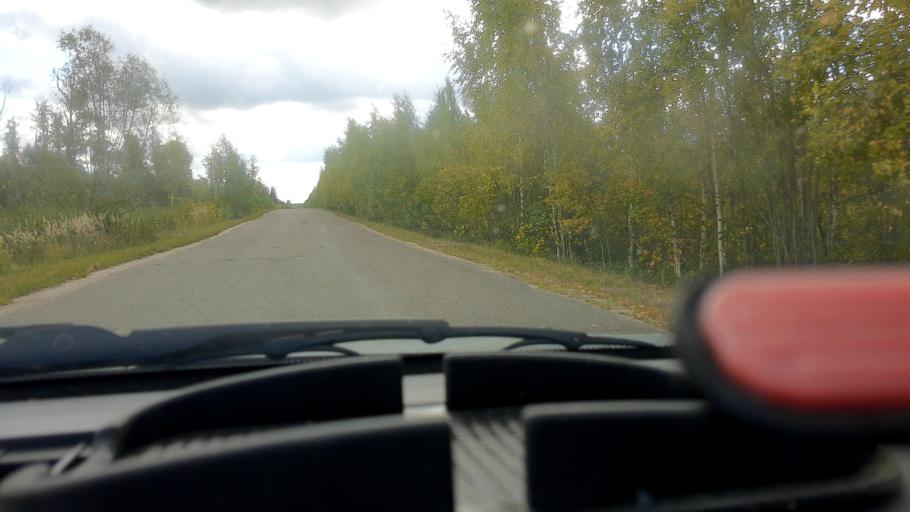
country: RU
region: Mariy-El
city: Kilemary
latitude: 56.8999
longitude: 46.7439
